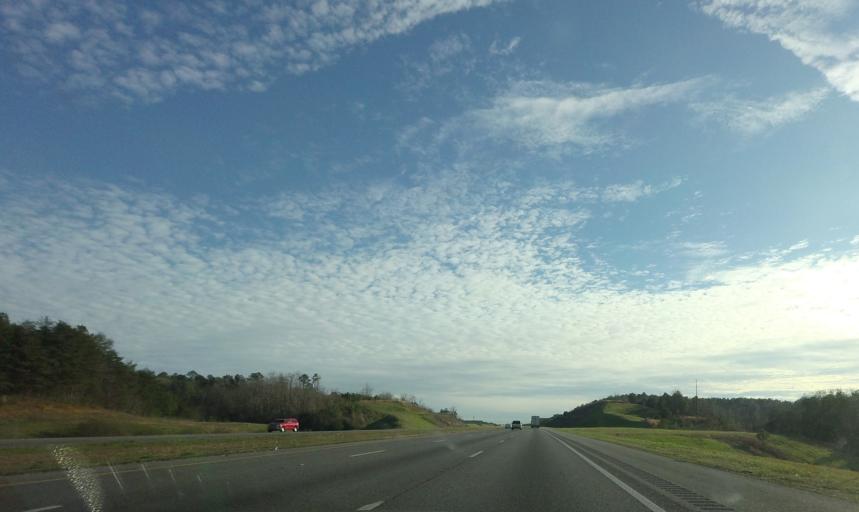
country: US
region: Alabama
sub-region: Walker County
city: Cordova
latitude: 33.7687
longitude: -87.2079
